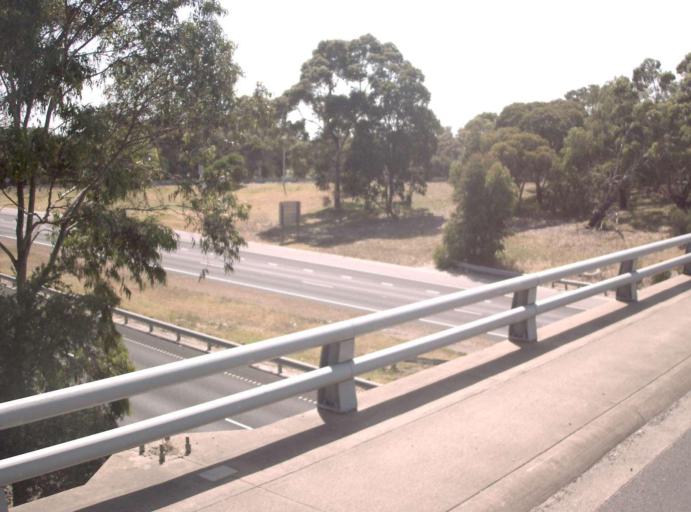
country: AU
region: Victoria
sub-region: Frankston
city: Seaford
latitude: -38.1087
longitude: 145.1389
